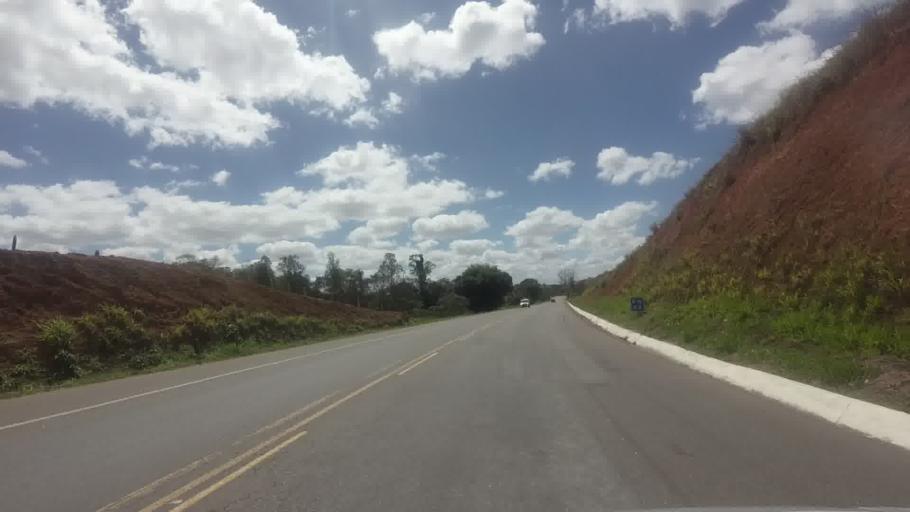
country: BR
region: Minas Gerais
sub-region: Recreio
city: Recreio
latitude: -21.6564
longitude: -42.3696
